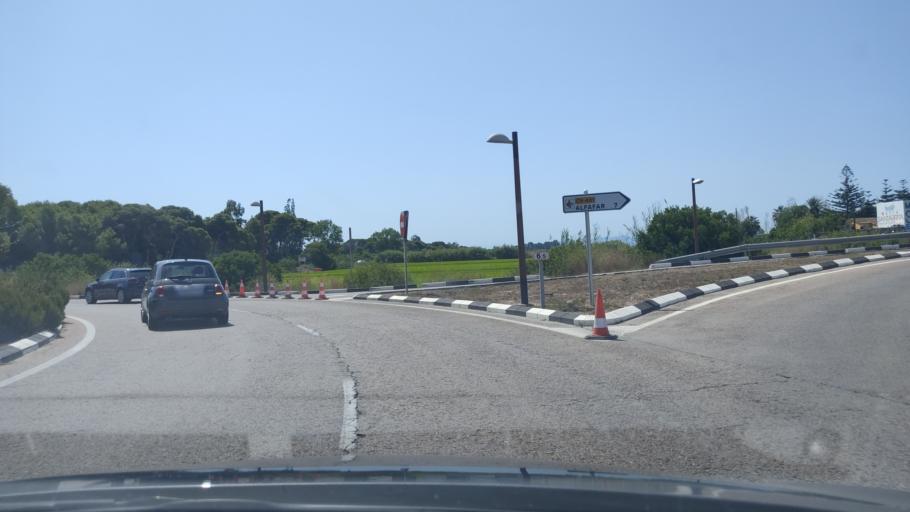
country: ES
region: Valencia
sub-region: Provincia de Valencia
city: Alfafar
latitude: 39.3766
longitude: -0.3329
